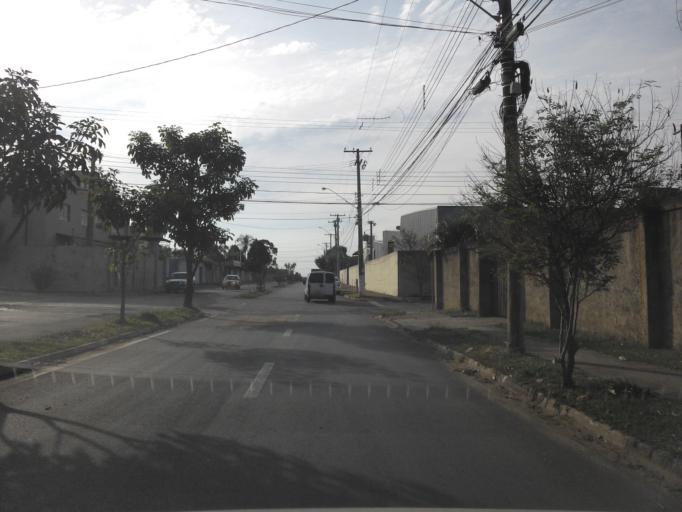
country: BR
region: Sao Paulo
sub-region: Hortolandia
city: Hortolandia
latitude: -22.9111
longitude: -47.2082
